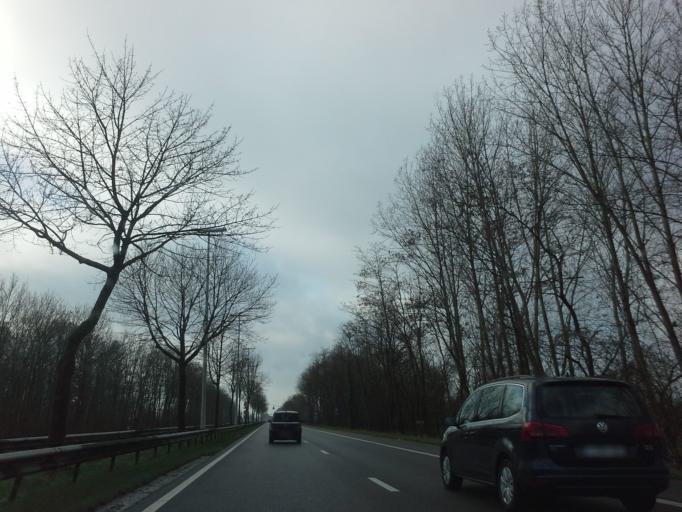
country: BE
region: Flanders
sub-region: Provincie Limburg
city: Nieuwerkerken
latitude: 50.8585
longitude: 5.2499
